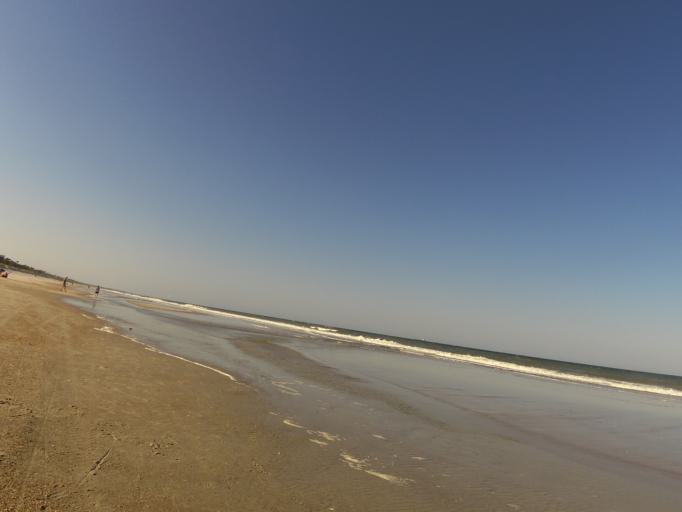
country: US
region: Florida
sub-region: Duval County
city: Atlantic Beach
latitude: 30.3375
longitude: -81.3955
